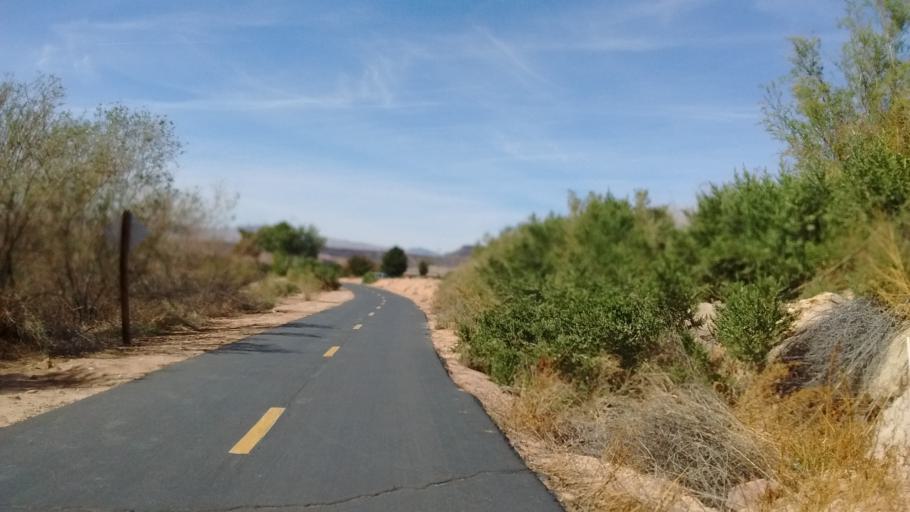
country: US
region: Utah
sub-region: Washington County
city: Saint George
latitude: 37.0870
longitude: -113.5587
